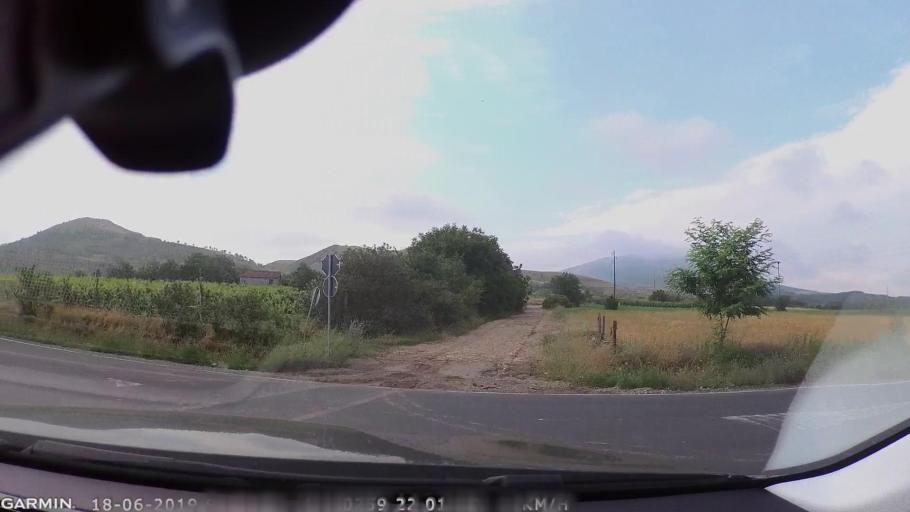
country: MK
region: Sveti Nikole
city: Sveti Nikole
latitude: 41.8050
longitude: 22.0180
